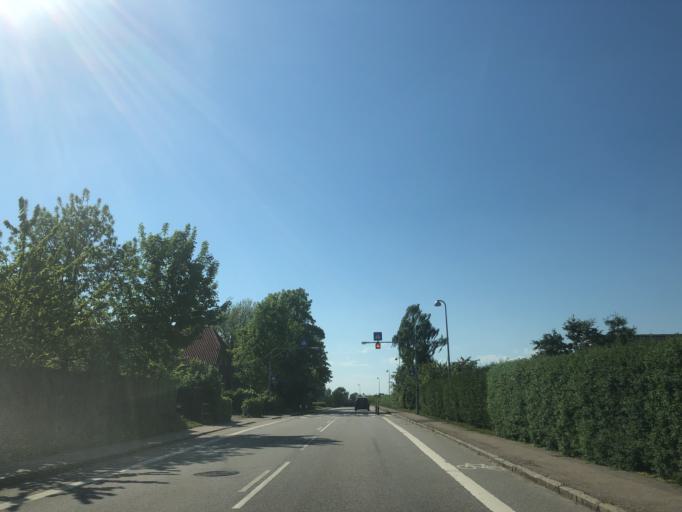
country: DK
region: Zealand
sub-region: Solrod Kommune
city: Havdrup
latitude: 55.5692
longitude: 12.0889
